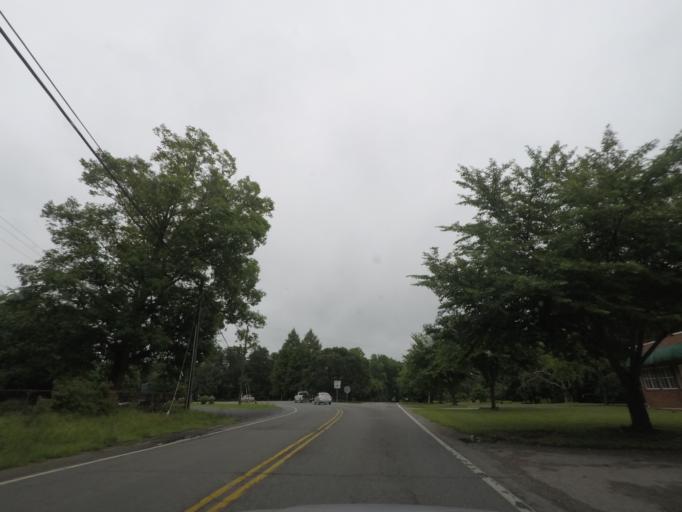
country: US
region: Virginia
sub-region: Fluvanna County
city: Weber City
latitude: 37.7814
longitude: -78.2362
